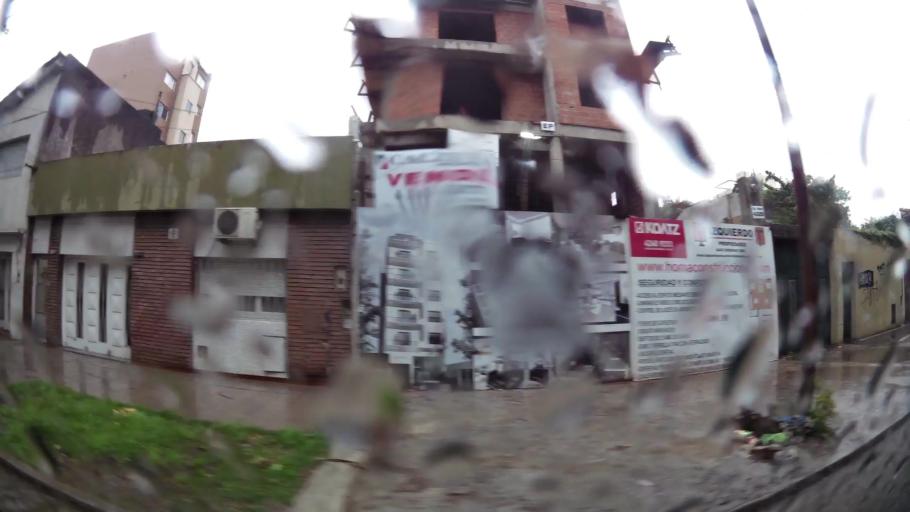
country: AR
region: Buenos Aires
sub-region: Partido de Lanus
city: Lanus
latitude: -34.7236
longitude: -58.3972
